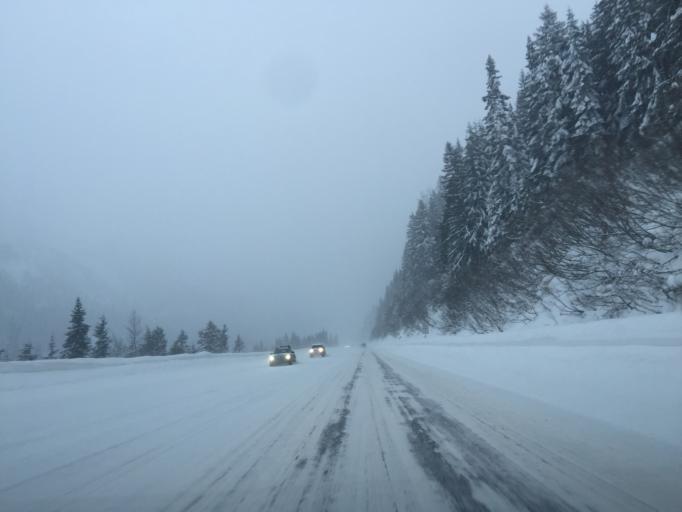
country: US
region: Washington
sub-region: Chelan County
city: Leavenworth
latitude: 47.7473
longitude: -121.1162
